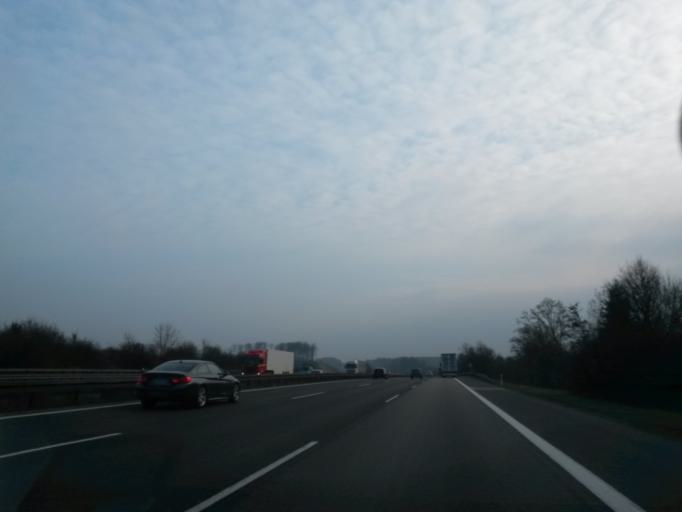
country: DE
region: Bavaria
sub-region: Upper Bavaria
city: Denkendorf
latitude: 48.8998
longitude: 11.4689
